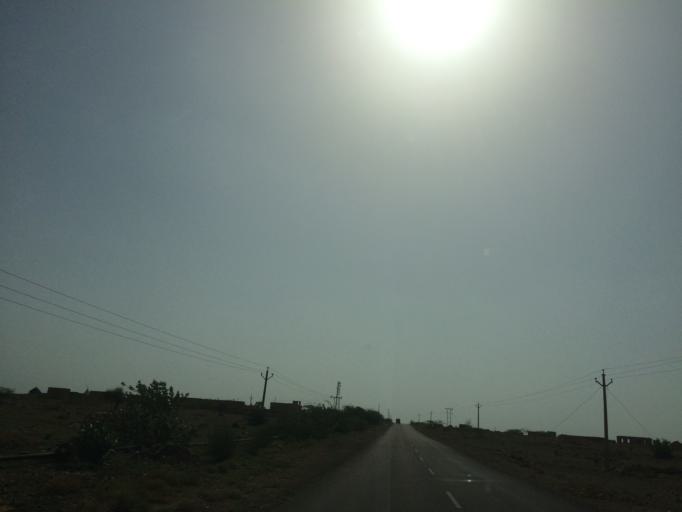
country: IN
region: Rajasthan
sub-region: Jaisalmer
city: Jaisalmer
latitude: 26.9195
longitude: 70.8362
